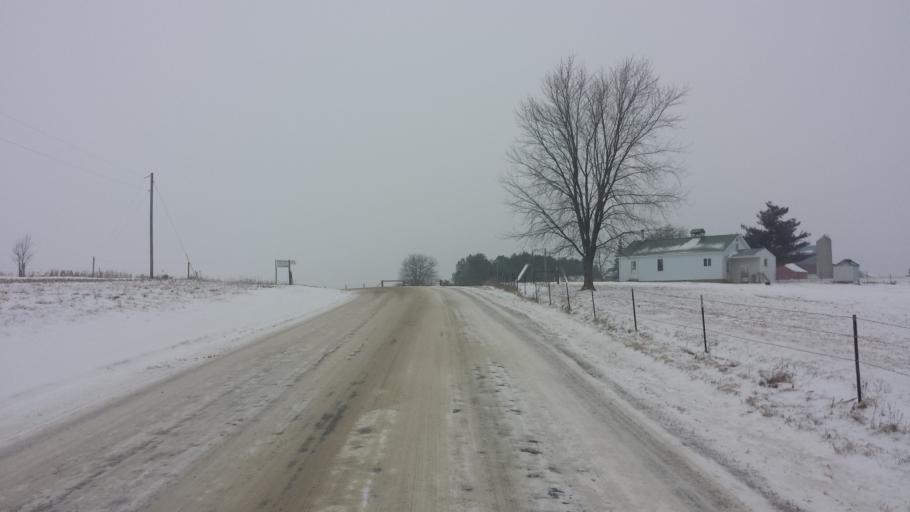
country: US
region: Wisconsin
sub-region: Monroe County
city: Cashton
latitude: 43.7099
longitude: -90.7044
